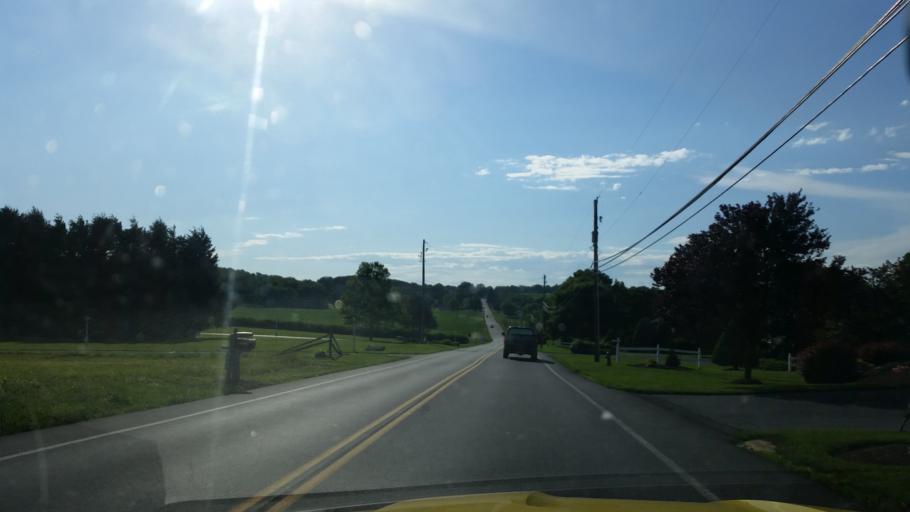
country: US
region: Pennsylvania
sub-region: Lancaster County
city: Brickerville
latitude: 40.2994
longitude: -76.3102
